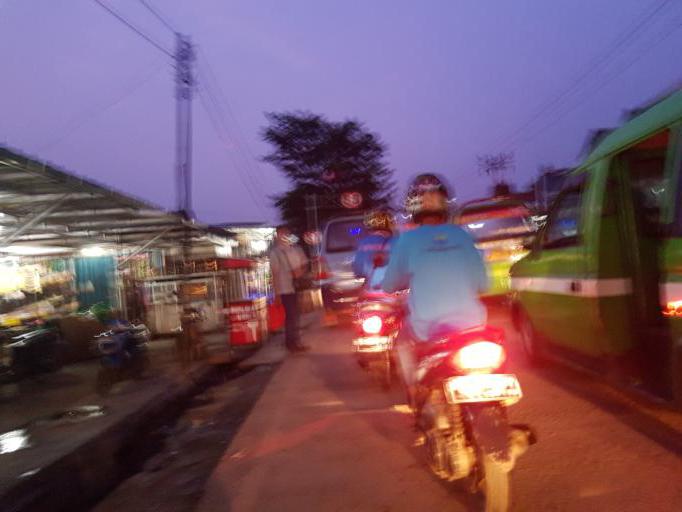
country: ID
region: West Java
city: Serpong
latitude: -6.3197
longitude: 106.6636
